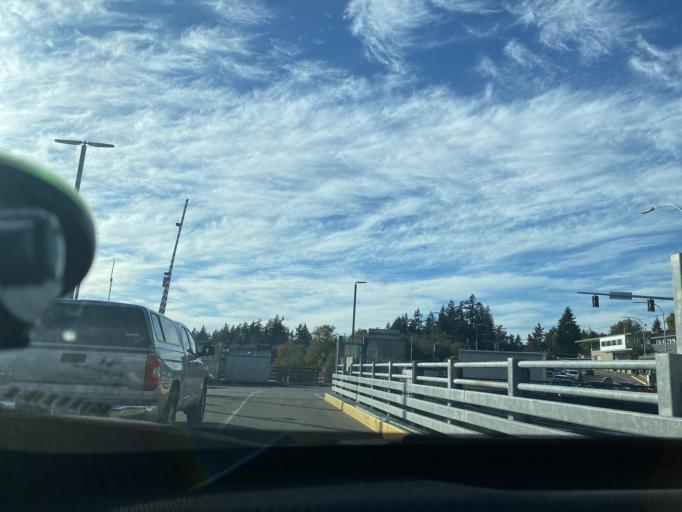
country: US
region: Washington
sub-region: Kitsap County
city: Bainbridge Island
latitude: 47.6221
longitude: -122.5097
